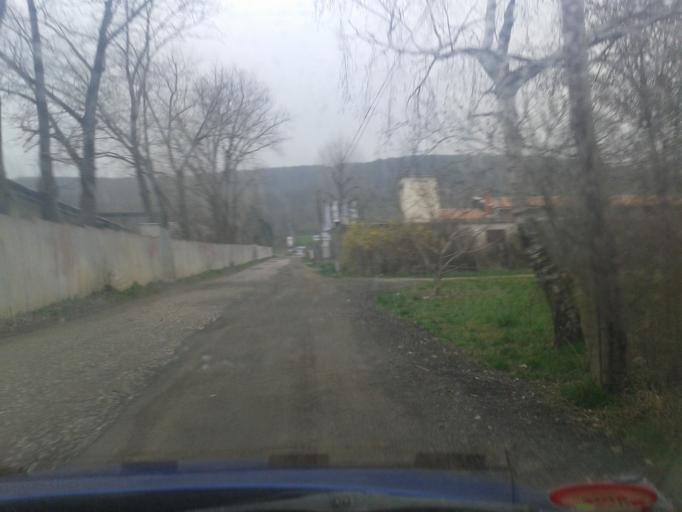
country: CZ
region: Central Bohemia
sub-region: Okres Beroun
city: Kraluv Dvur
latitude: 49.9583
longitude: 14.0450
